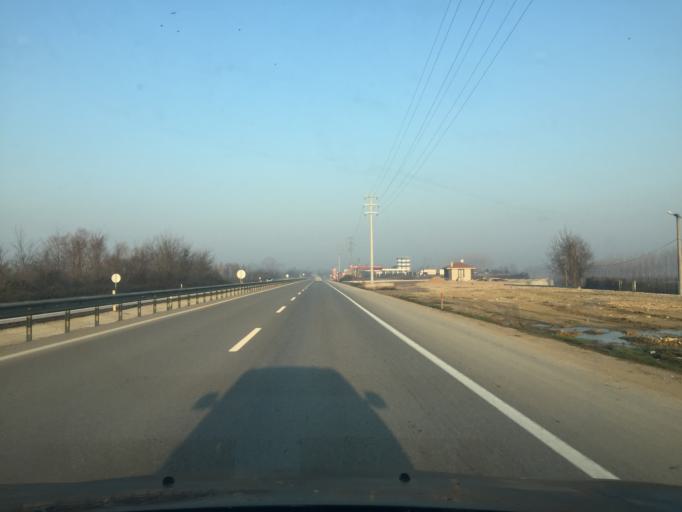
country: TR
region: Sakarya
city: Akyazi
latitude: 40.6768
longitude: 30.5828
